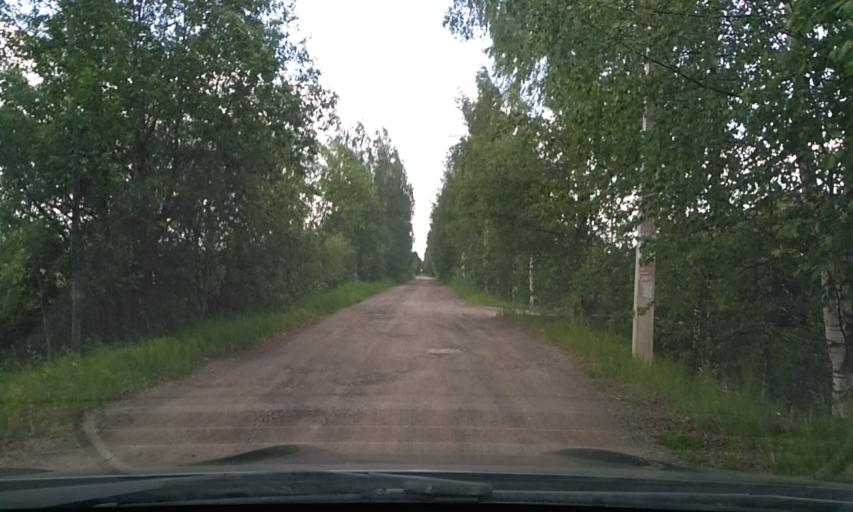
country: RU
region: Leningrad
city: Otradnoye
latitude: 59.8142
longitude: 30.8257
